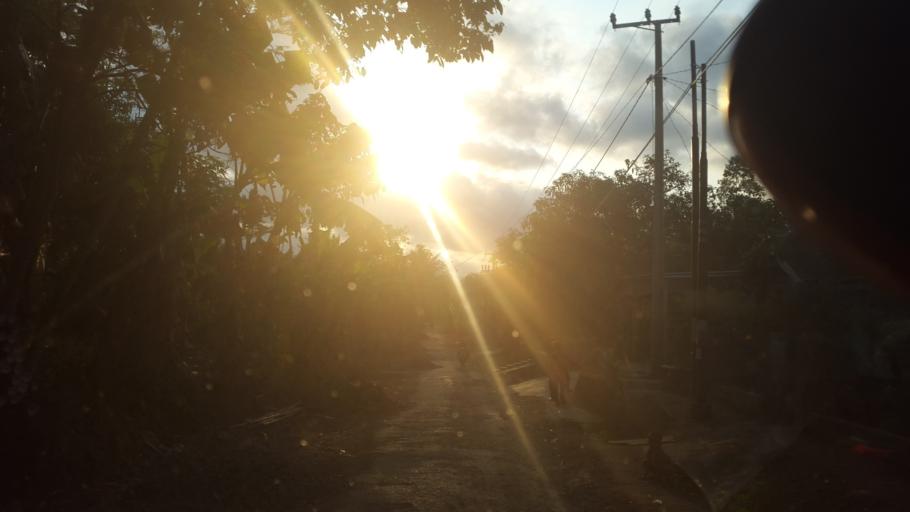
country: ID
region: West Java
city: Datarnangka
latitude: -7.2125
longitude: 106.8618
